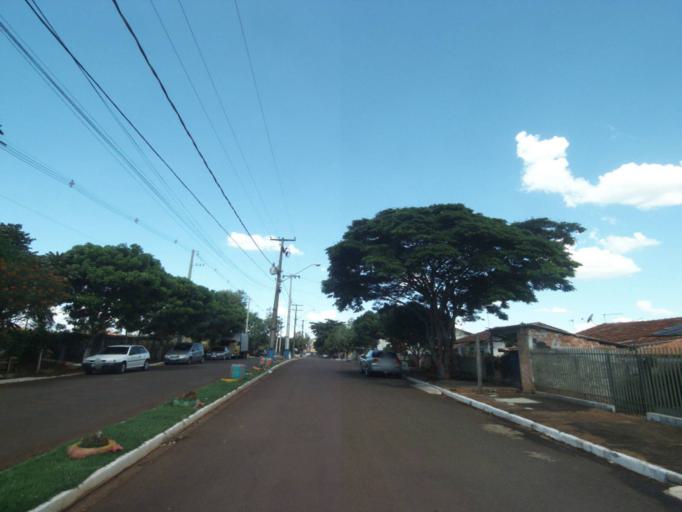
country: BR
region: Parana
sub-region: Sertanopolis
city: Sertanopolis
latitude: -23.0449
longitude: -50.8235
